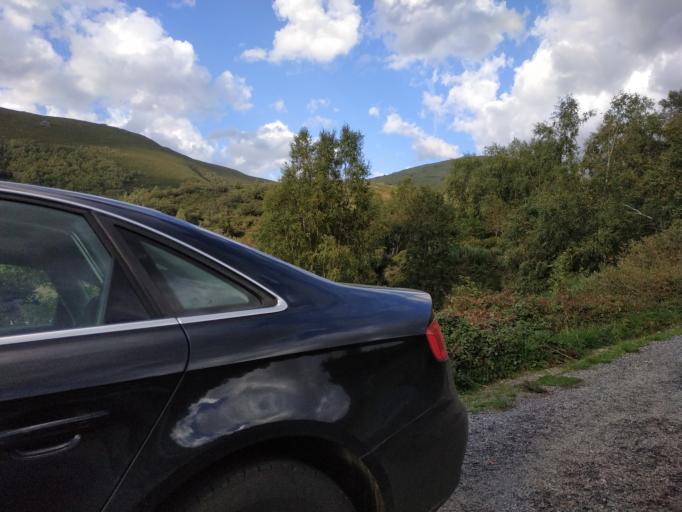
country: ES
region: Castille and Leon
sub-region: Provincia de Leon
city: Candin
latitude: 42.8651
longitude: -6.8506
